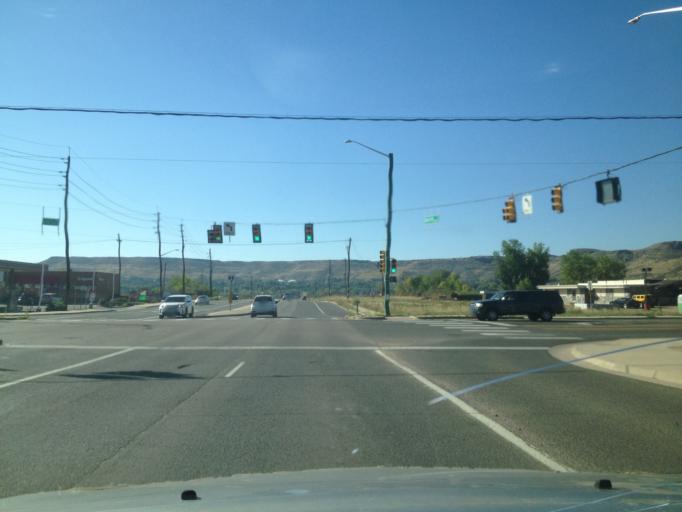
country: US
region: Colorado
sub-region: Jefferson County
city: Applewood
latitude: 39.7765
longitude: -105.1749
